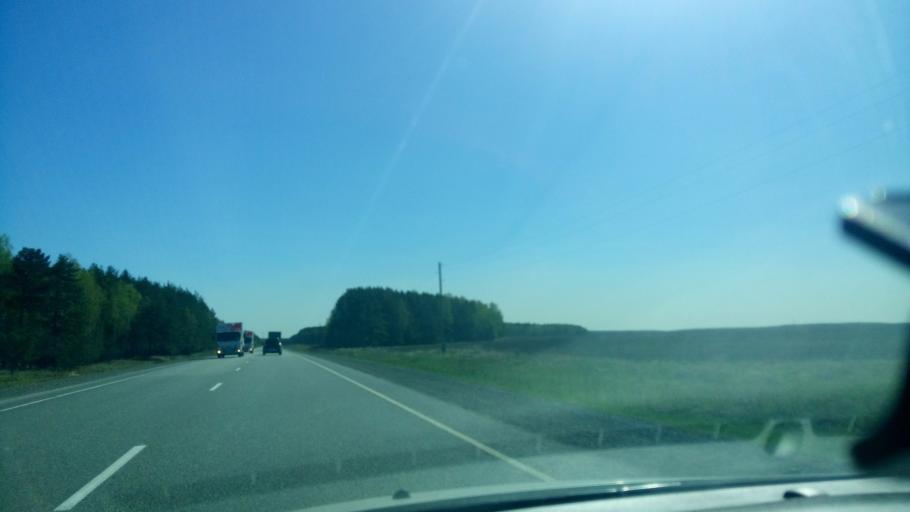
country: RU
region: Sverdlovsk
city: Gryaznovskoye
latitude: 56.7854
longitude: 61.6764
